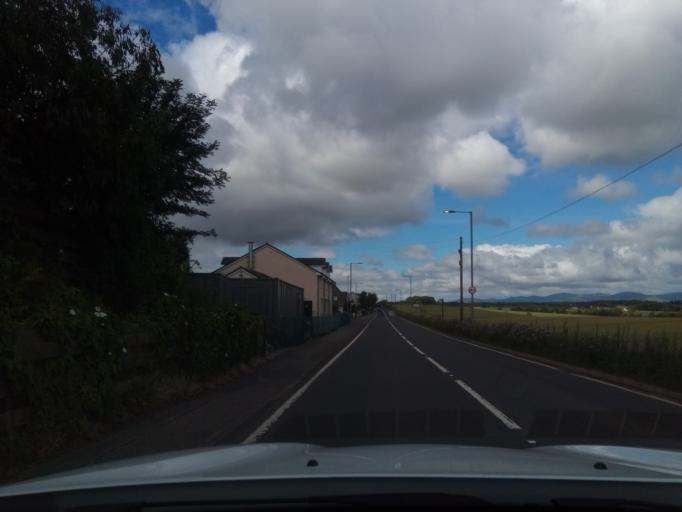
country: GB
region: Scotland
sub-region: Fife
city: Cairneyhill
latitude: 56.0489
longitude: -3.5261
